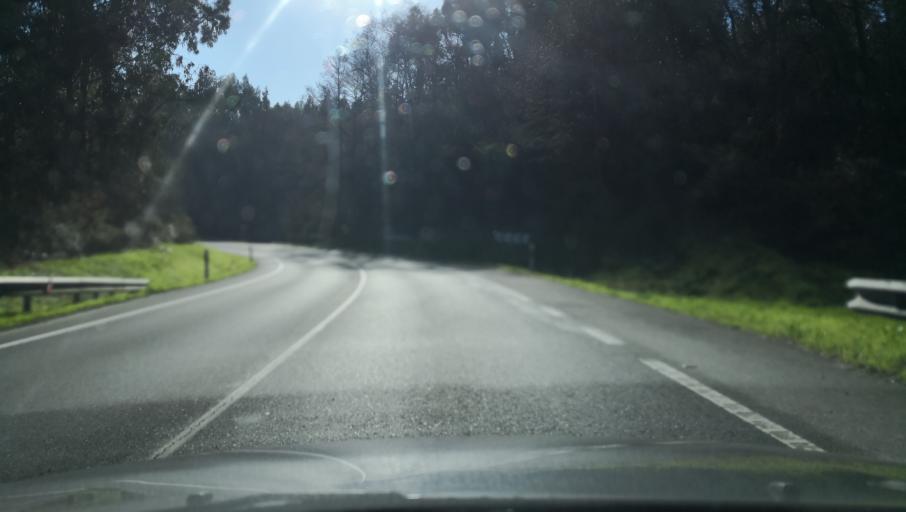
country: ES
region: Galicia
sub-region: Provincia de Pontevedra
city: Silleda
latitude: 42.7440
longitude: -8.3380
